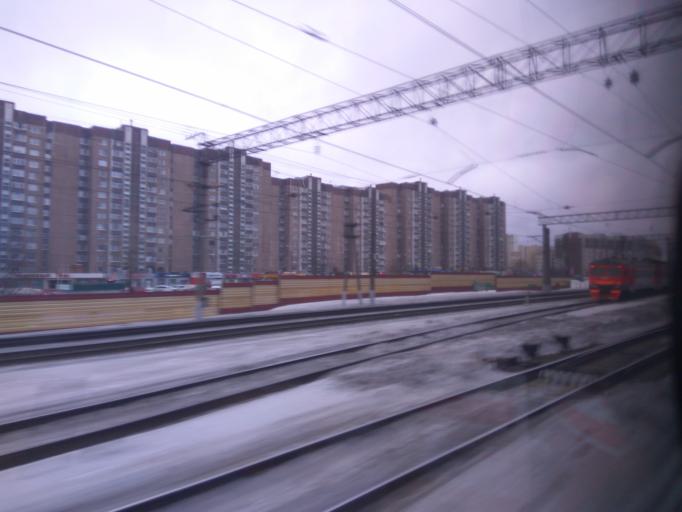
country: RU
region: Moscow
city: Zelenograd
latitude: 55.9819
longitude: 37.1712
